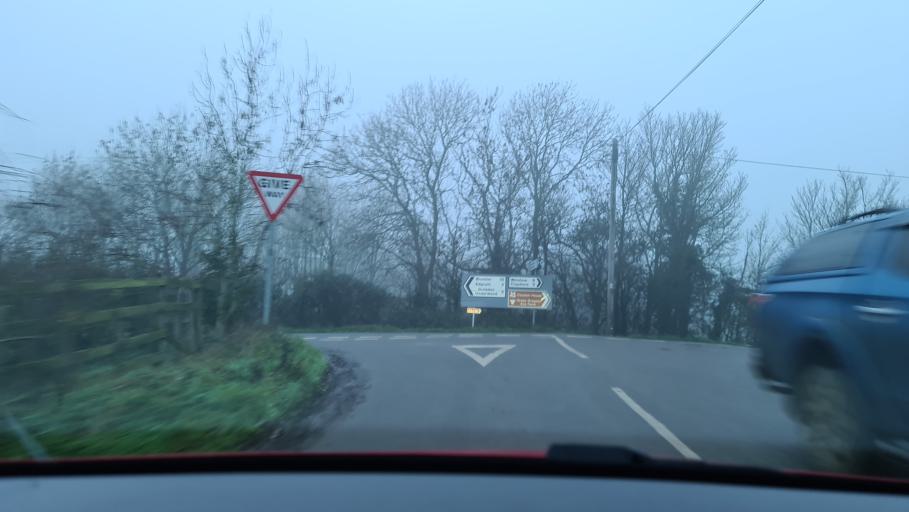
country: GB
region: England
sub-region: Buckinghamshire
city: Waddesdon
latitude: 51.8831
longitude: -0.9381
